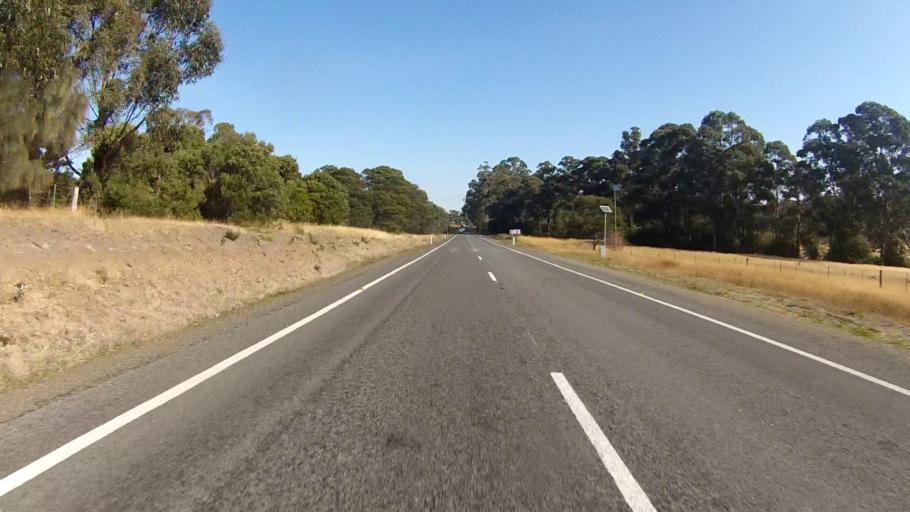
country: AU
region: Tasmania
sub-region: Sorell
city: Sorell
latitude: -42.6944
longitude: 147.5264
